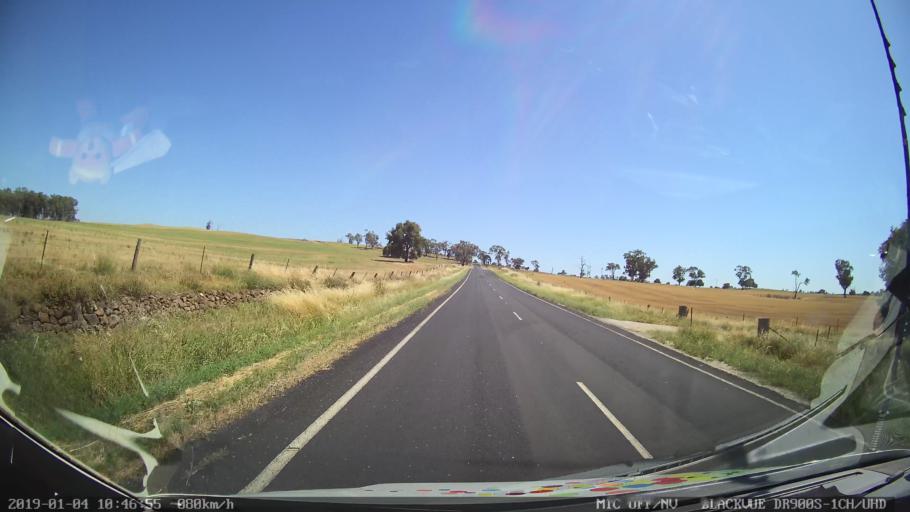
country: AU
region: New South Wales
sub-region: Cabonne
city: Molong
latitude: -33.2755
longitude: 148.7209
